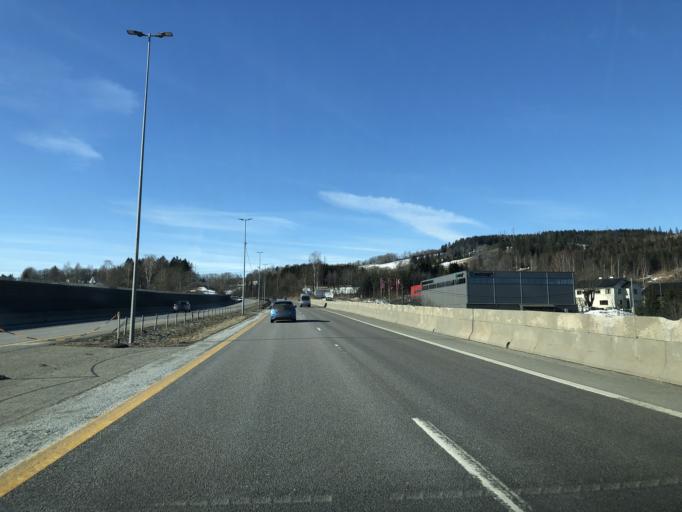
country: NO
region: Buskerud
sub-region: Lier
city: Tranby
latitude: 59.8184
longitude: 10.3290
